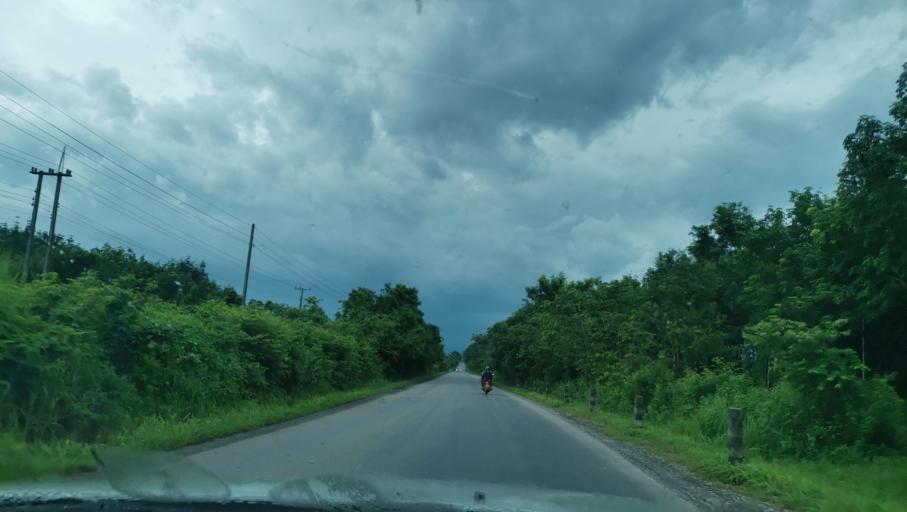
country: TH
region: Nakhon Phanom
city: Ban Phaeng
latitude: 17.8547
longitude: 104.4312
